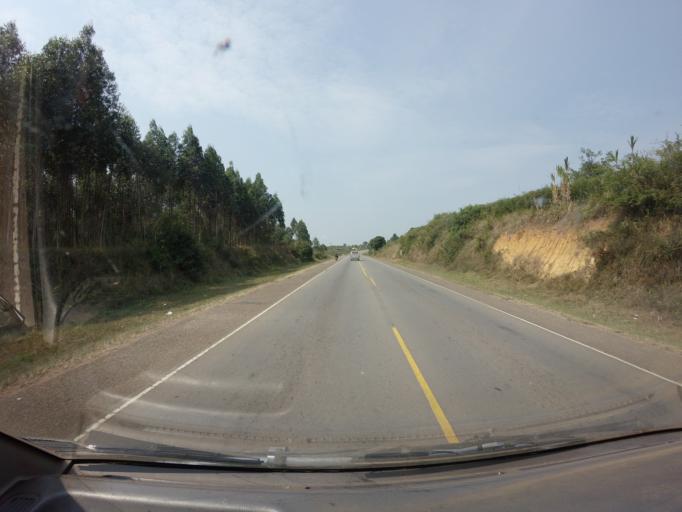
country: UG
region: Central Region
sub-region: Lwengo District
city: Lwengo
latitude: -0.3997
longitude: 31.3956
